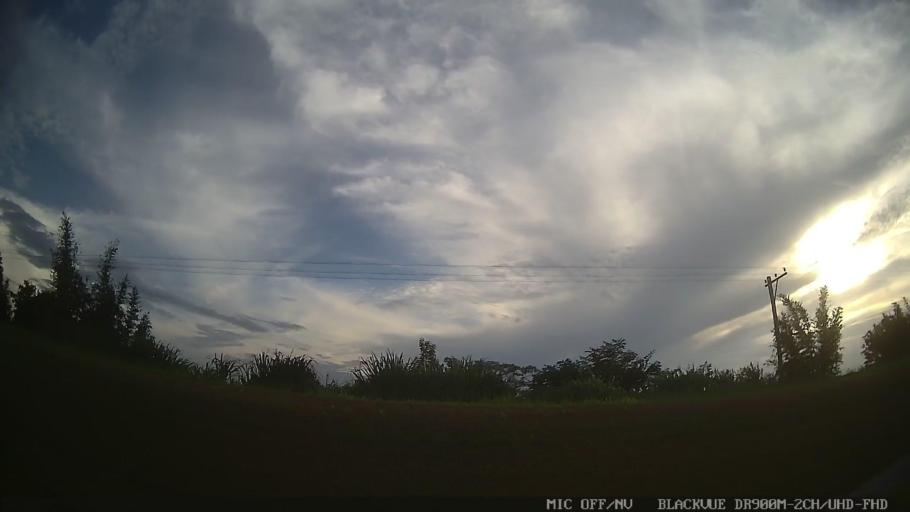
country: BR
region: Sao Paulo
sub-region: Porto Feliz
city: Porto Feliz
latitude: -23.1985
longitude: -47.6128
